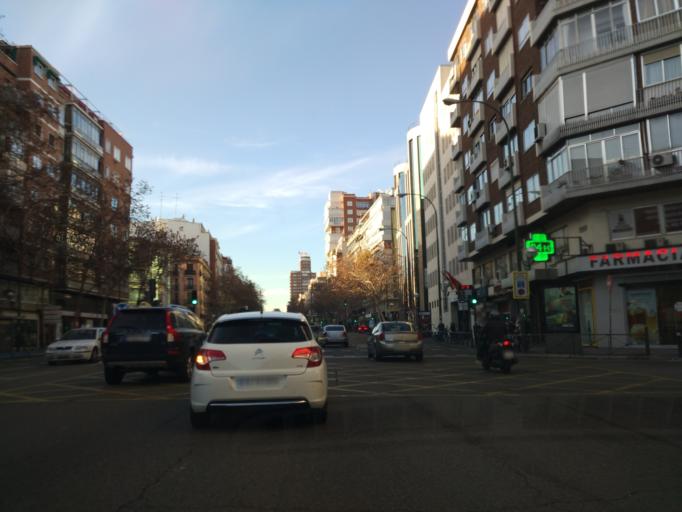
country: ES
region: Madrid
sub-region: Provincia de Madrid
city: Salamanca
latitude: 40.4326
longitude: -3.6725
